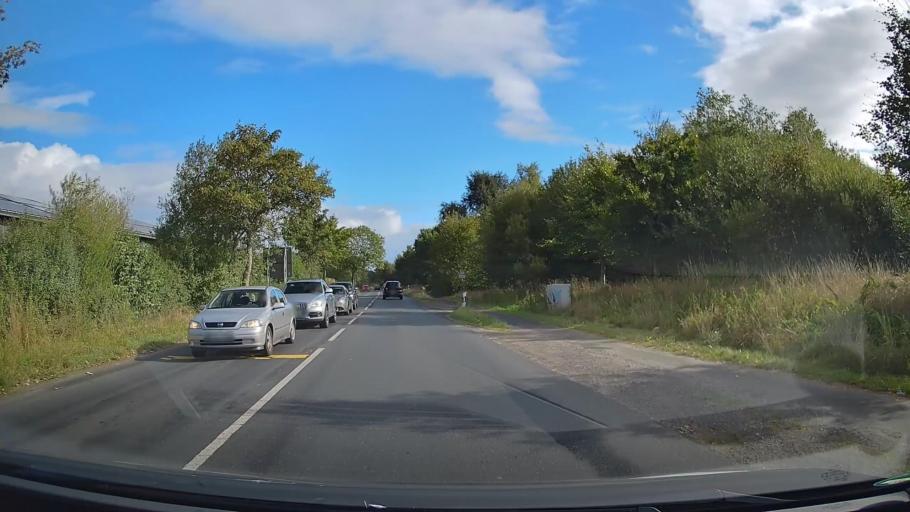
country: DE
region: Lower Saxony
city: Loxstedt
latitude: 53.4440
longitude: 8.5882
